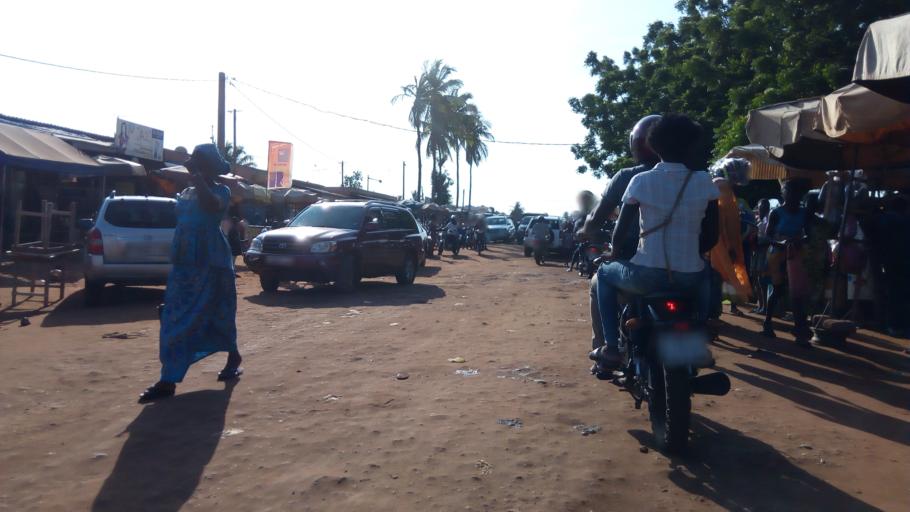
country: TG
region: Maritime
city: Lome
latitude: 6.2300
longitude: 1.1968
